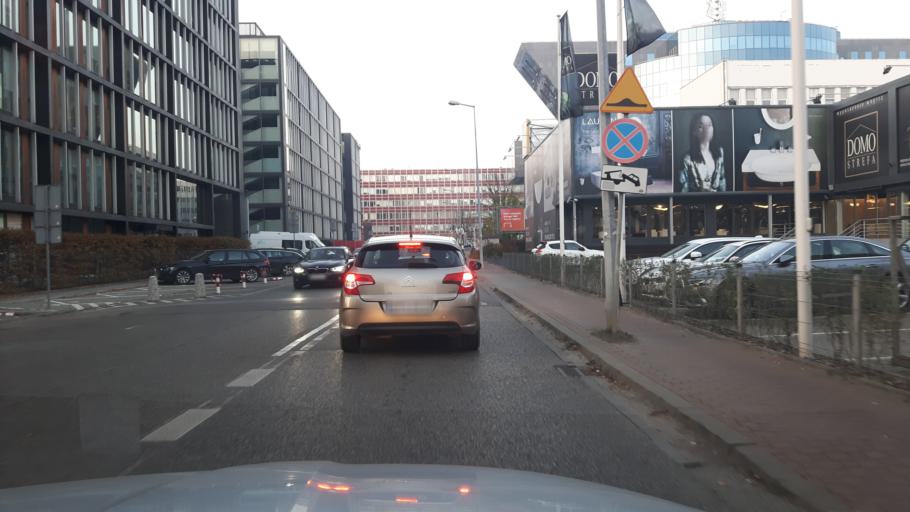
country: PL
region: Masovian Voivodeship
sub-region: Warszawa
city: Mokotow
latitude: 52.1816
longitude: 21.0060
